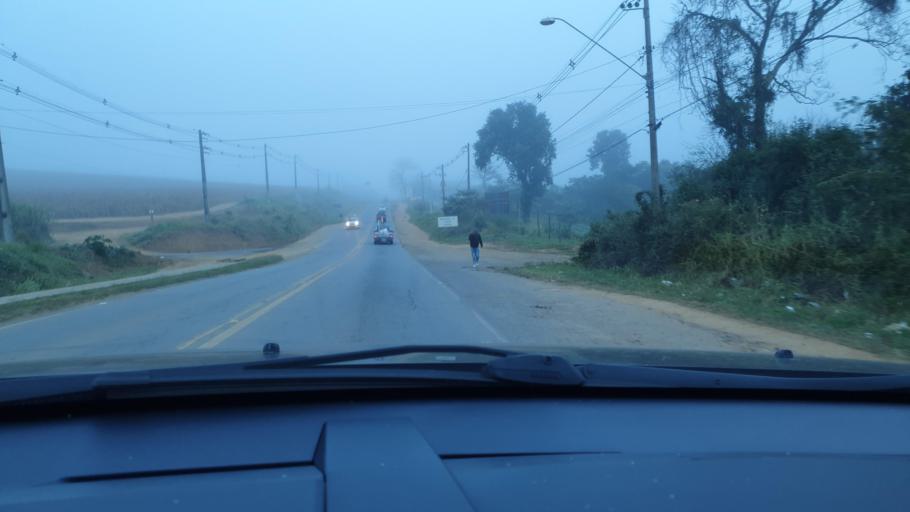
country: BR
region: Sao Paulo
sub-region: Ibiuna
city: Ibiuna
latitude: -23.6681
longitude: -47.2293
